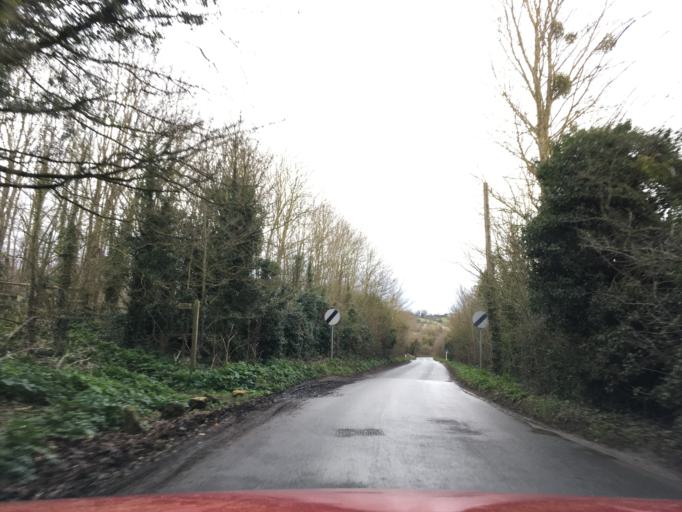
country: GB
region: England
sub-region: Gloucestershire
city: Gotherington
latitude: 52.0224
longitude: -2.0337
